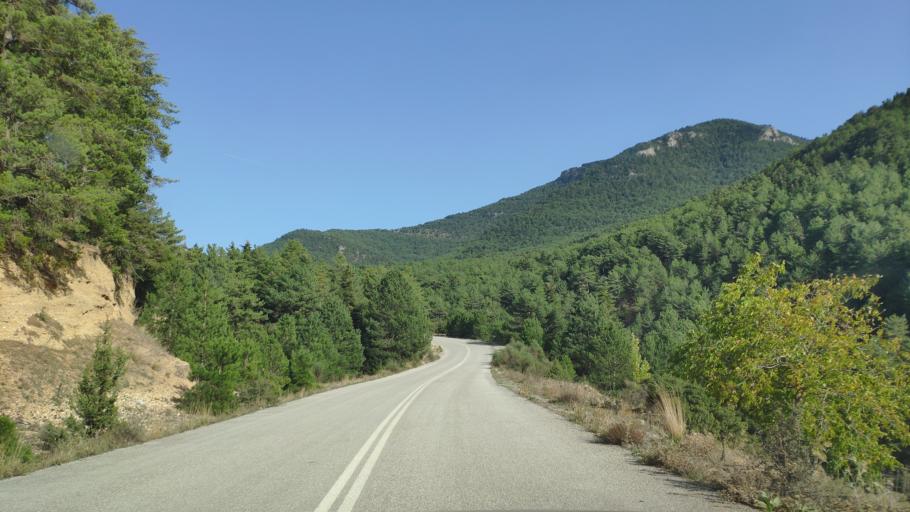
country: GR
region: West Greece
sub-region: Nomos Achaias
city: Aiyira
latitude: 37.9937
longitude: 22.3709
